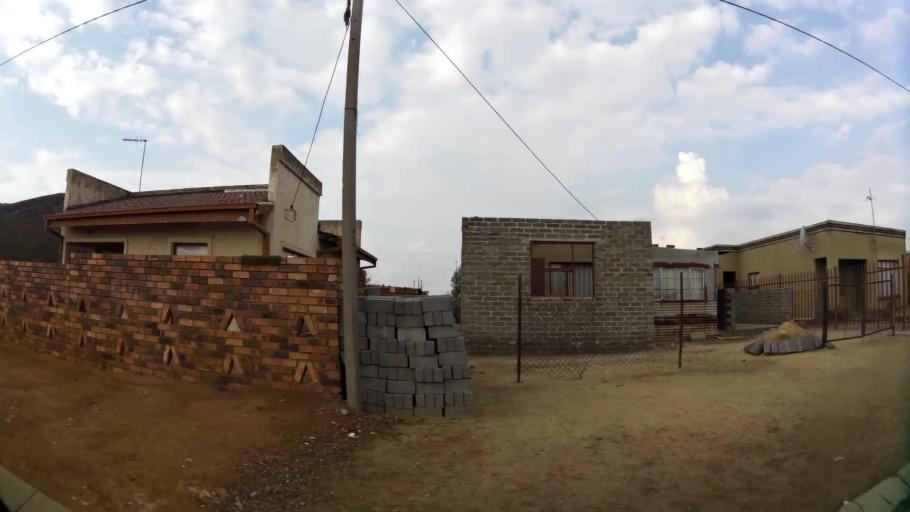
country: ZA
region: Gauteng
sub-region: Sedibeng District Municipality
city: Vanderbijlpark
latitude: -26.6770
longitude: 27.8586
